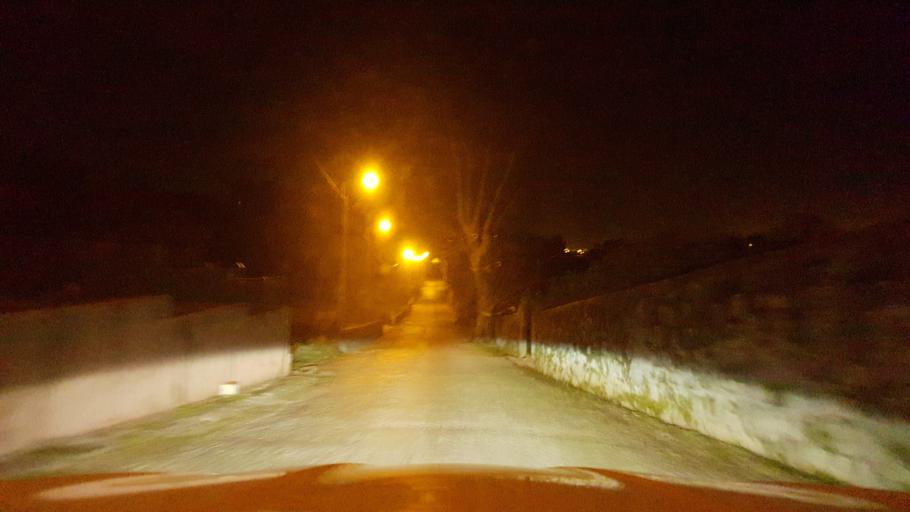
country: PT
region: Porto
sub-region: Matosinhos
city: Santa Cruz do Bispo
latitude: 41.2202
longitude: -8.6678
